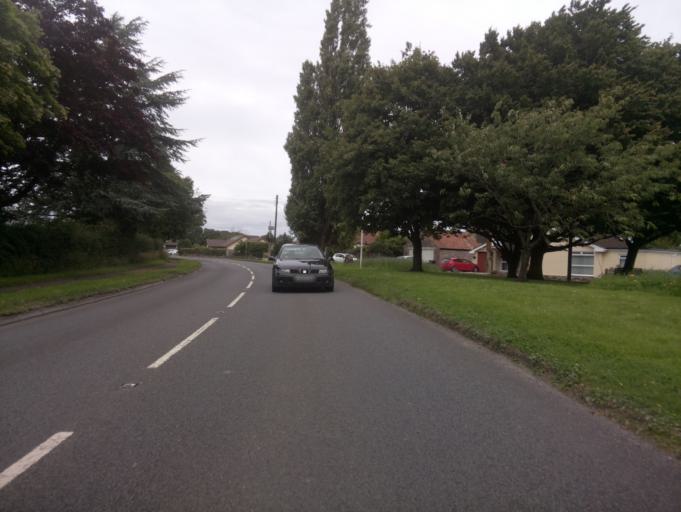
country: GB
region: England
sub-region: North Somerset
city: Kenn
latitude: 51.4158
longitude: -2.8417
